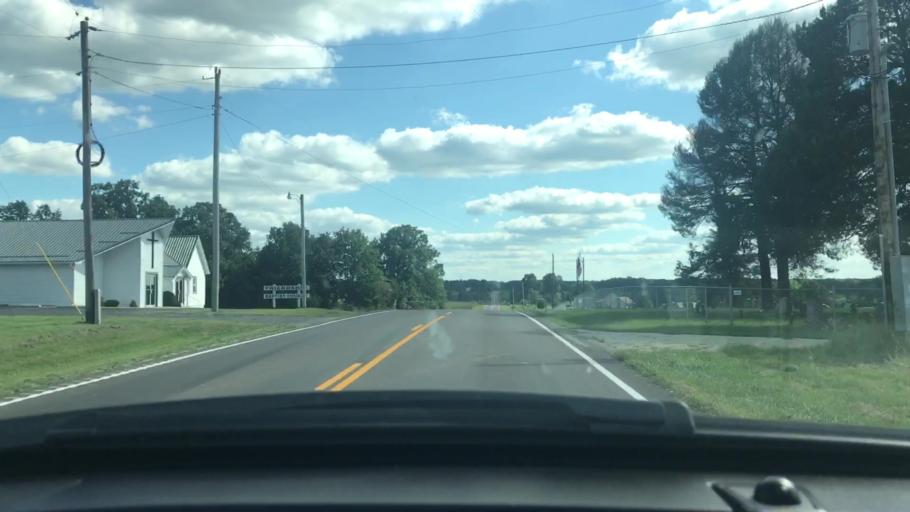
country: US
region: Missouri
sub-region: Wright County
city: Mountain Grove
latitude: 37.2471
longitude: -92.3003
